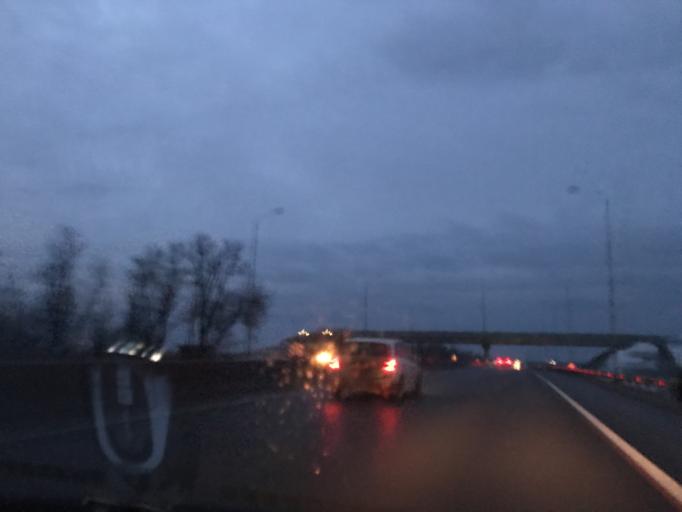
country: RU
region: Rostov
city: Samarskoye
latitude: 46.9685
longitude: 39.7199
